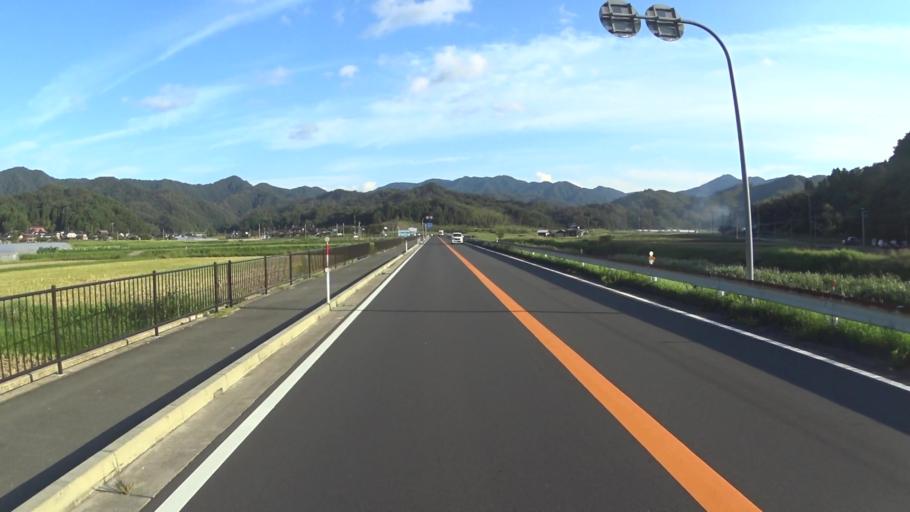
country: JP
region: Hyogo
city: Toyooka
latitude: 35.5776
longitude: 134.9738
